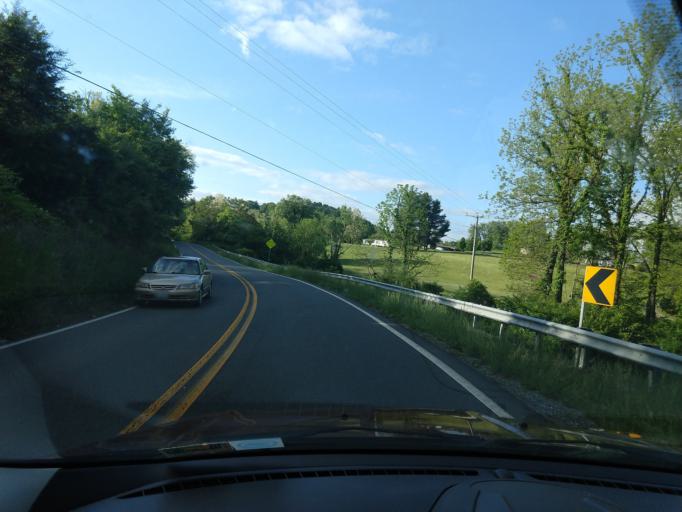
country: US
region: Virginia
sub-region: Wythe County
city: Wytheville
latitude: 36.8997
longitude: -80.9704
